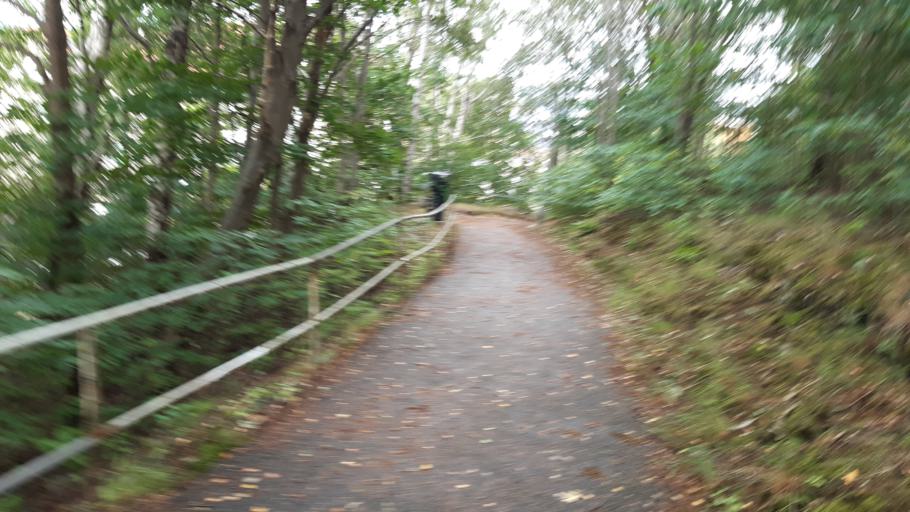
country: SE
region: Vaestra Goetaland
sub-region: Goteborg
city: Eriksbo
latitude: 57.7222
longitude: 12.0332
